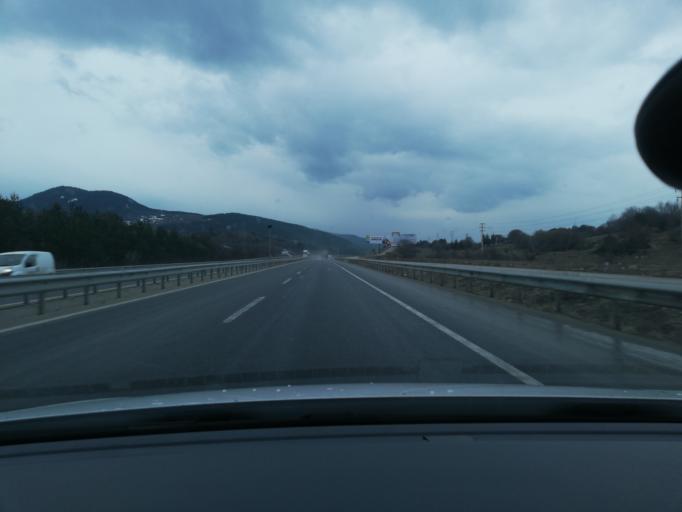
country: TR
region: Bolu
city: Yenicaga
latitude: 40.7547
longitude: 31.9114
